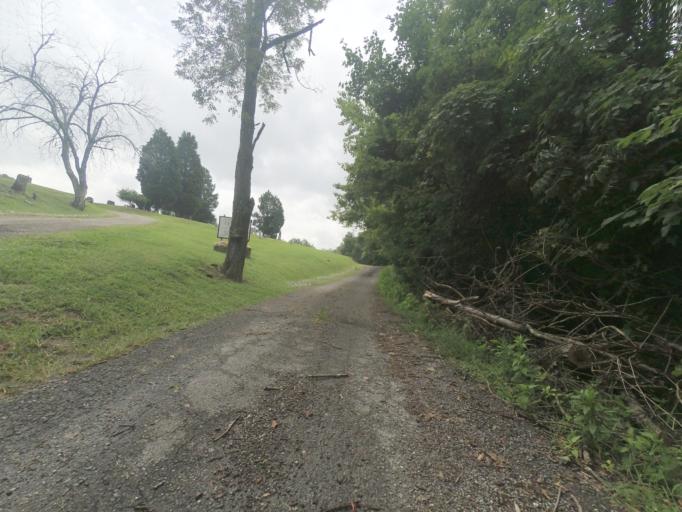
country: US
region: West Virginia
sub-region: Cabell County
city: Huntington
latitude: 38.4309
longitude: -82.4655
